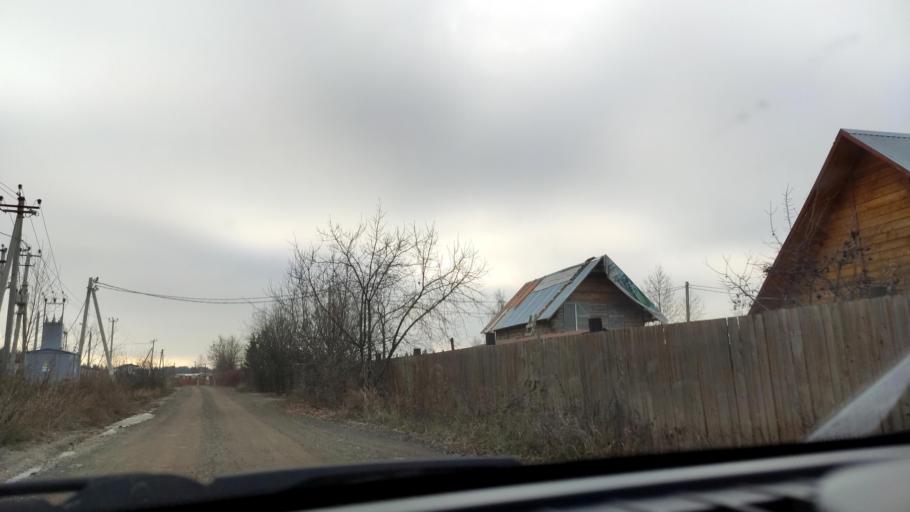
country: RU
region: Perm
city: Kondratovo
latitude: 57.9549
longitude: 56.1713
